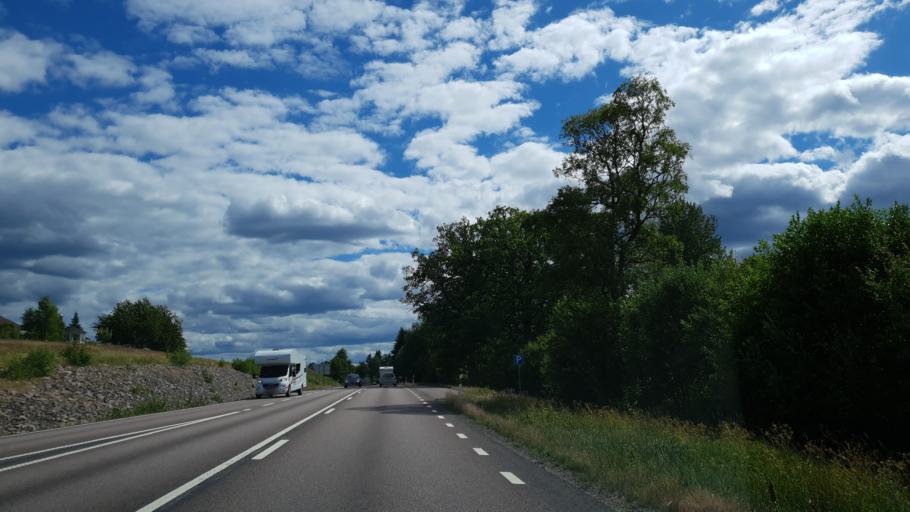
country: SE
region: Kronoberg
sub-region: Lessebo Kommun
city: Lessebo
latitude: 56.8484
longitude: 15.3889
